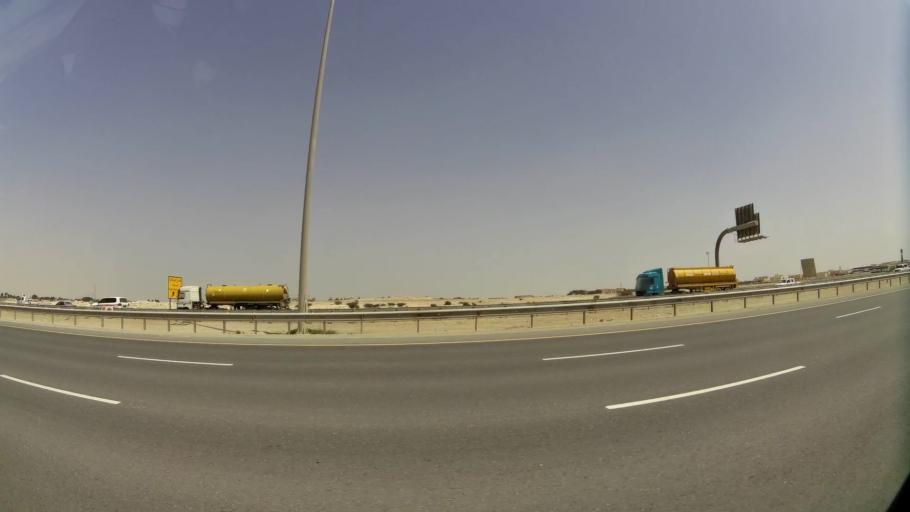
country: QA
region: Baladiyat Umm Salal
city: Umm Salal Muhammad
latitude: 25.4384
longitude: 51.4114
